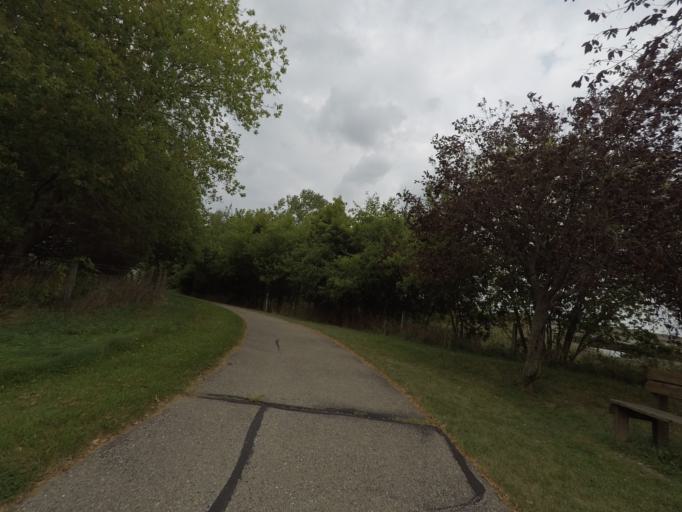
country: US
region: Wisconsin
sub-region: Jefferson County
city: Lake Koshkonong
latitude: 42.8887
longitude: -88.8725
